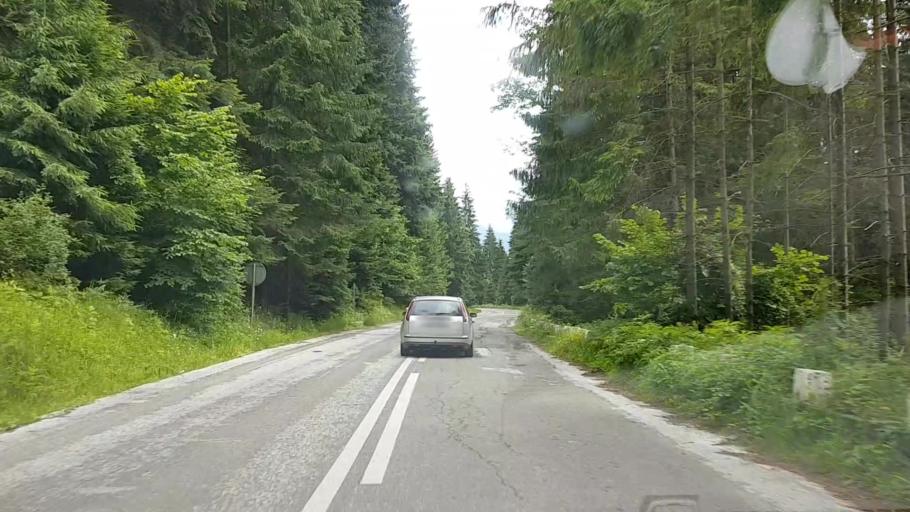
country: RO
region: Neamt
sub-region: Comuna Pangarati
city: Pangarati
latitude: 46.9690
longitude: 26.1168
